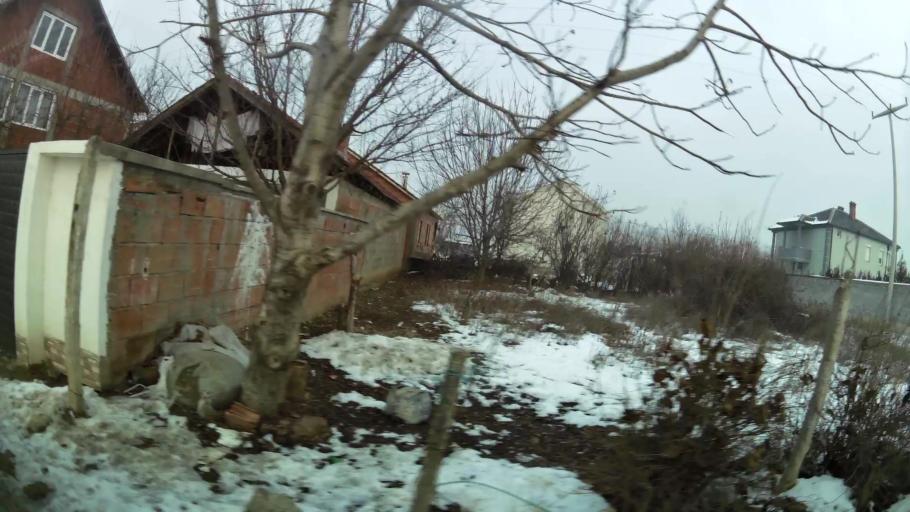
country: MK
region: Suto Orizari
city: Suto Orizare
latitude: 42.0379
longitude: 21.4152
